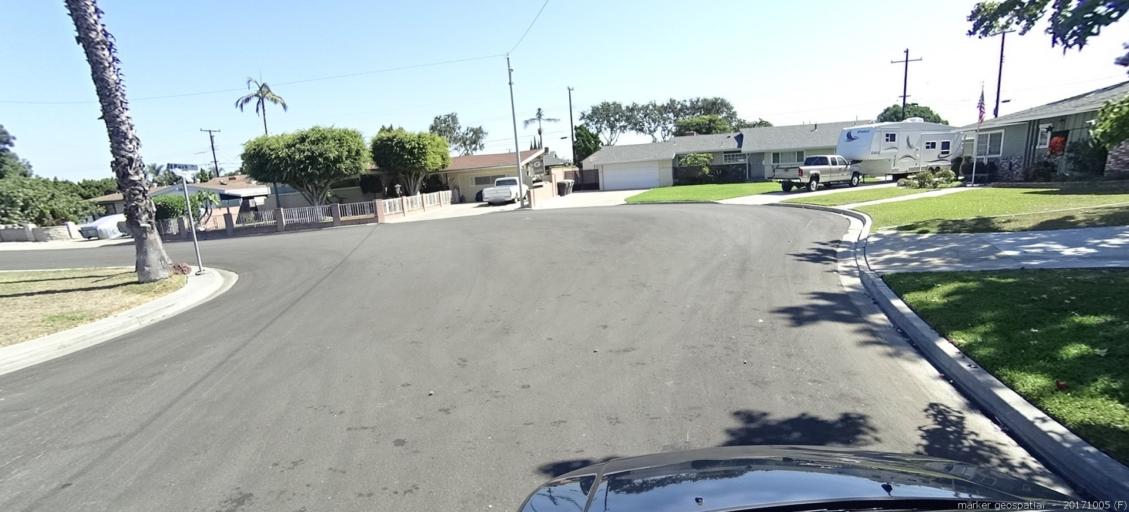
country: US
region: California
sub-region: Orange County
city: Stanton
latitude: 33.8005
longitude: -117.9725
